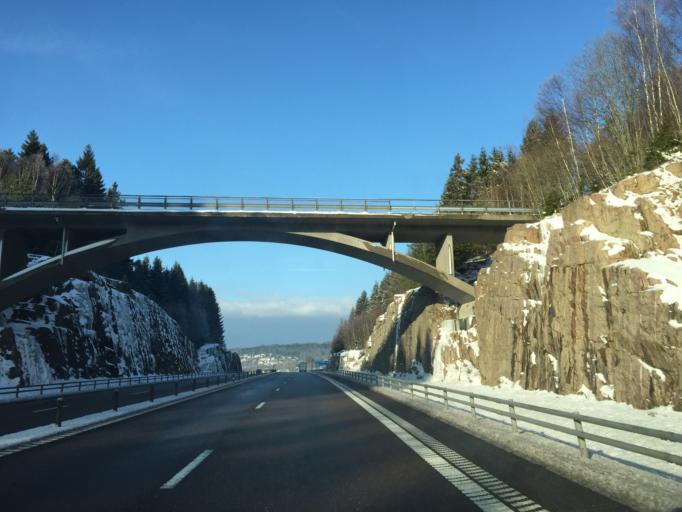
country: SE
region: Vaestra Goetaland
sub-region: Tanums Kommun
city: Tanumshede
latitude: 58.7306
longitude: 11.3364
